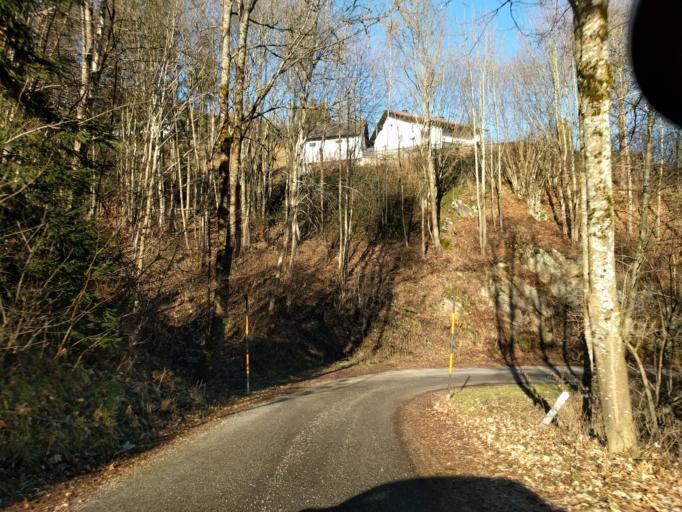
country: AT
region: Upper Austria
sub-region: Politischer Bezirk Urfahr-Umgebung
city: Kirchschlag bei Linz
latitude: 48.4098
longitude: 14.2903
